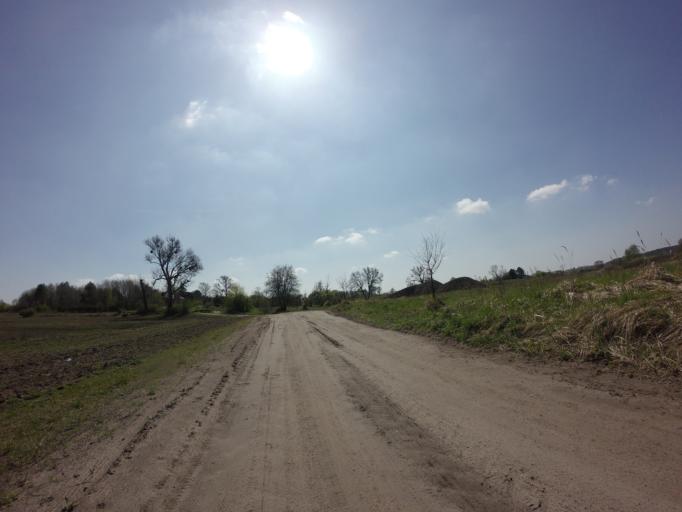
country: PL
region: West Pomeranian Voivodeship
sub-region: Powiat choszczenski
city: Choszczno
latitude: 53.1652
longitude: 15.4551
